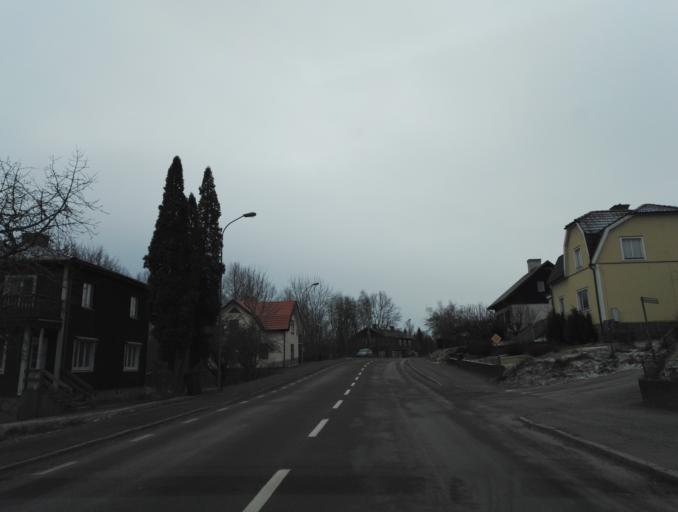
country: SE
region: Kalmar
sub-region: Hultsfreds Kommun
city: Virserum
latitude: 57.3106
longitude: 15.5853
